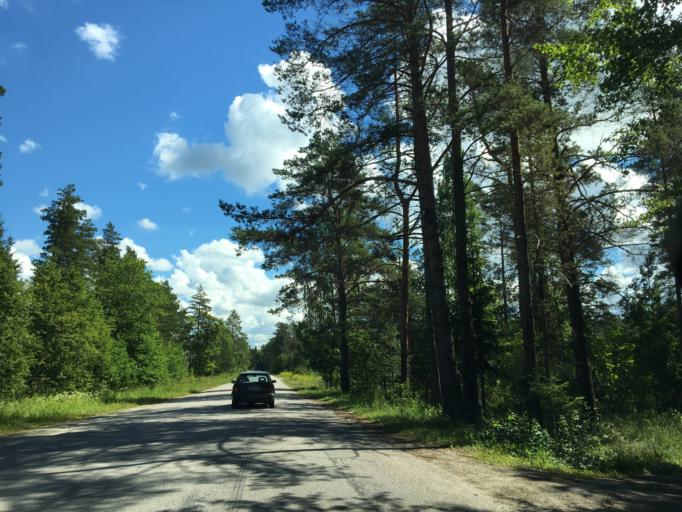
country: EE
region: Harju
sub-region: Nissi vald
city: Riisipere
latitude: 59.2439
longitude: 24.2791
